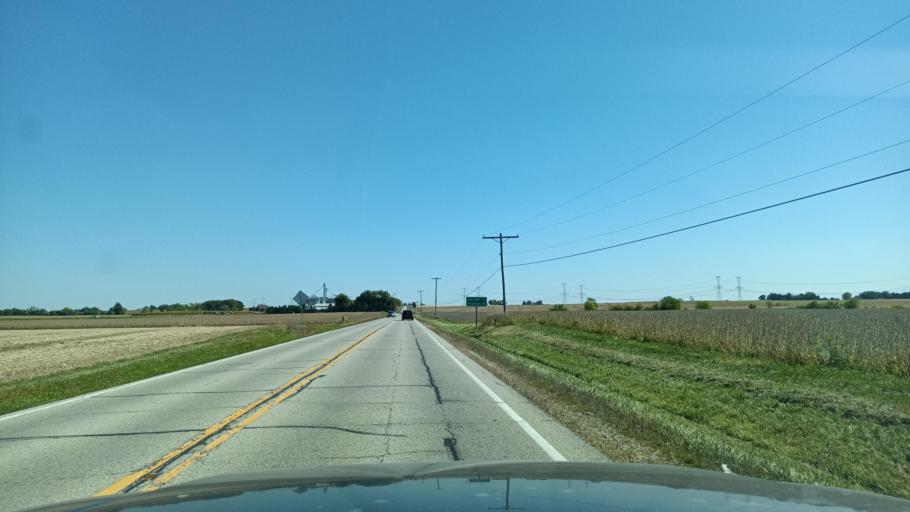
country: US
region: Illinois
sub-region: Tazewell County
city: Morton
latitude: 40.6134
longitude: -89.4283
